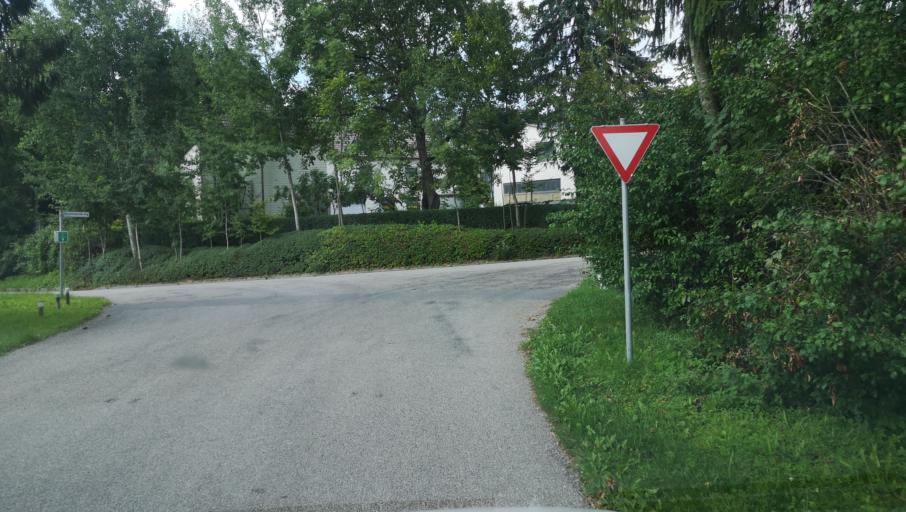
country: AT
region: Lower Austria
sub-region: Politischer Bezirk Amstetten
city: Zeillern
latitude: 48.1566
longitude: 14.8244
